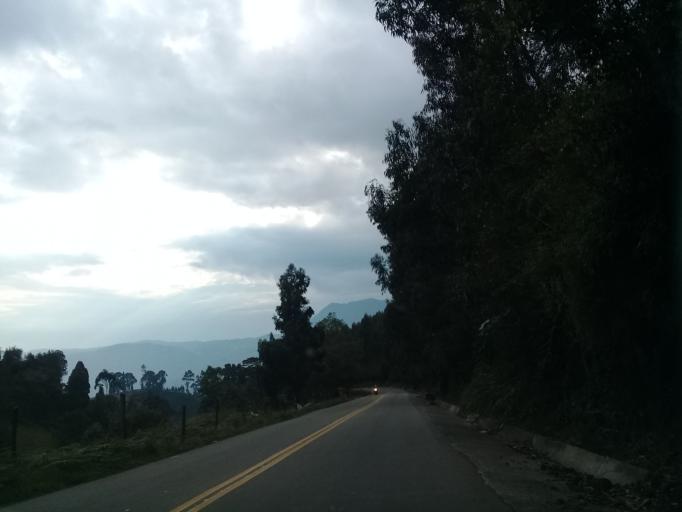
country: CO
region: Cundinamarca
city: Zipaquira
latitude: 5.0311
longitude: -74.0306
